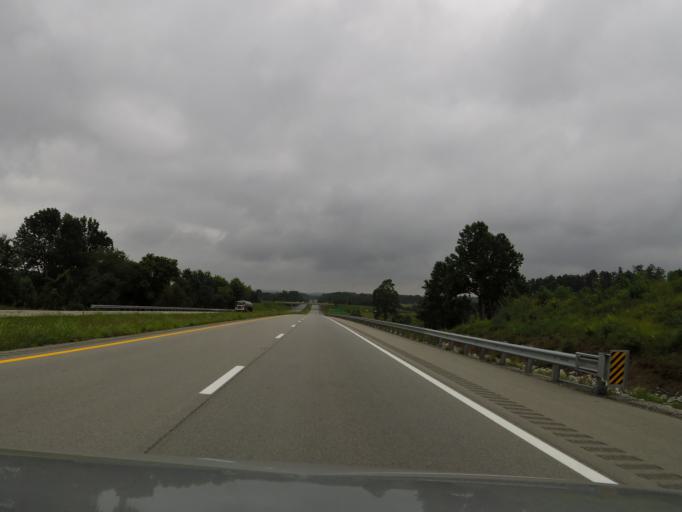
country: US
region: Kentucky
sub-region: Grayson County
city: Leitchfield
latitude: 37.4121
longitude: -86.4918
